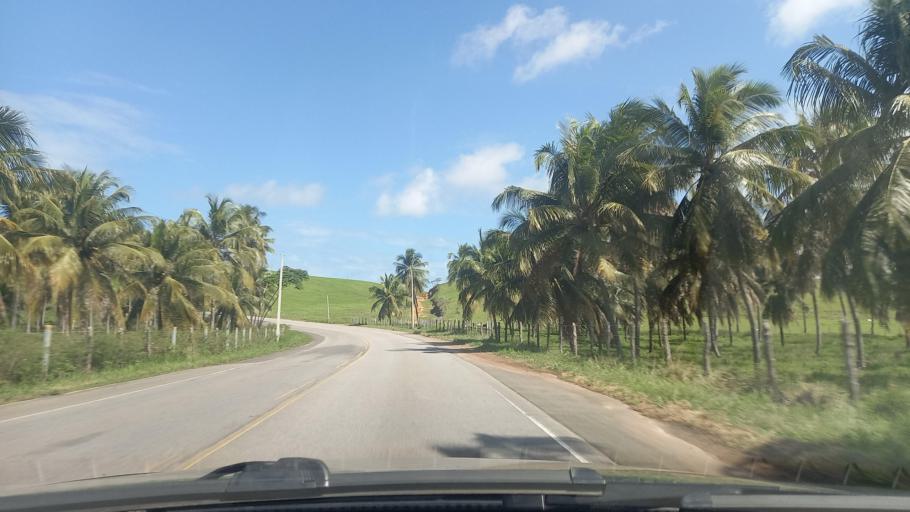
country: BR
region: Alagoas
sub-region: Marechal Deodoro
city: Marechal Deodoro
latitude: -9.8586
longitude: -35.9191
